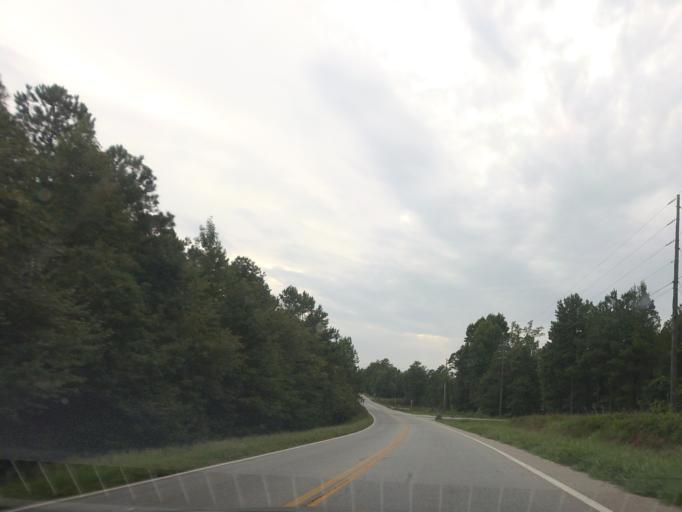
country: US
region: Georgia
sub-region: Twiggs County
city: Jeffersonville
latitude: 32.7655
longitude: -83.4721
